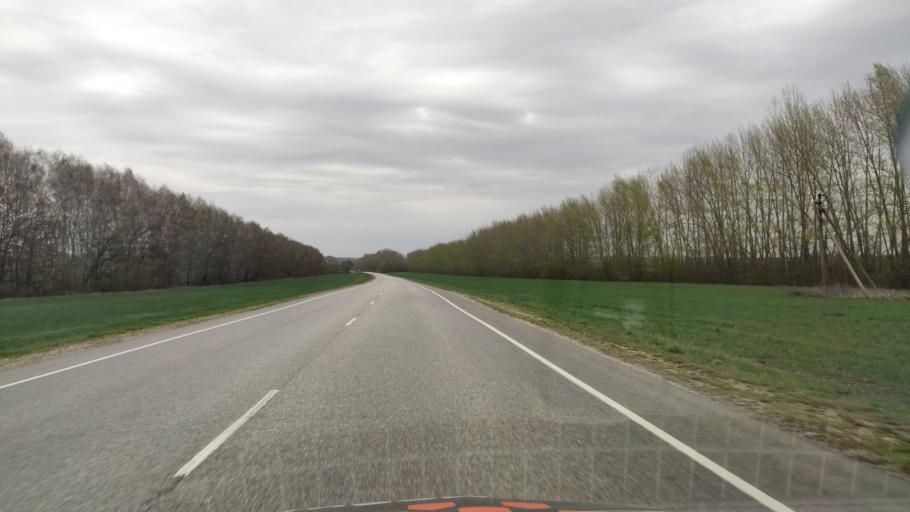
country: RU
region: Kursk
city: Olym
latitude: 51.5513
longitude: 38.2109
